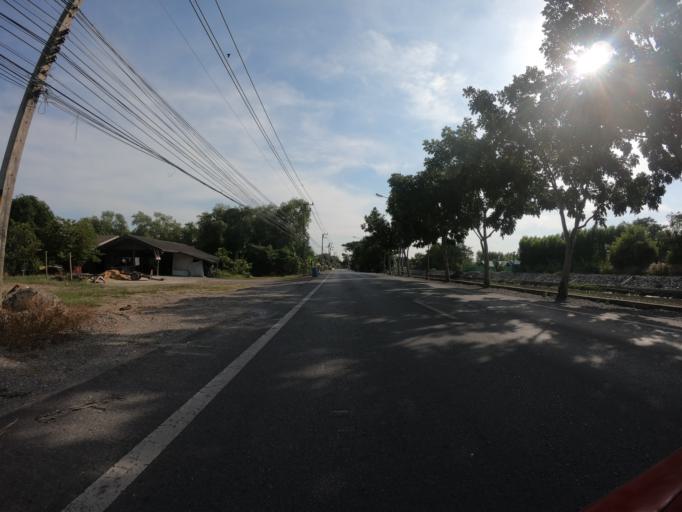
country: TH
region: Pathum Thani
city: Thanyaburi
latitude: 13.9787
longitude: 100.7290
